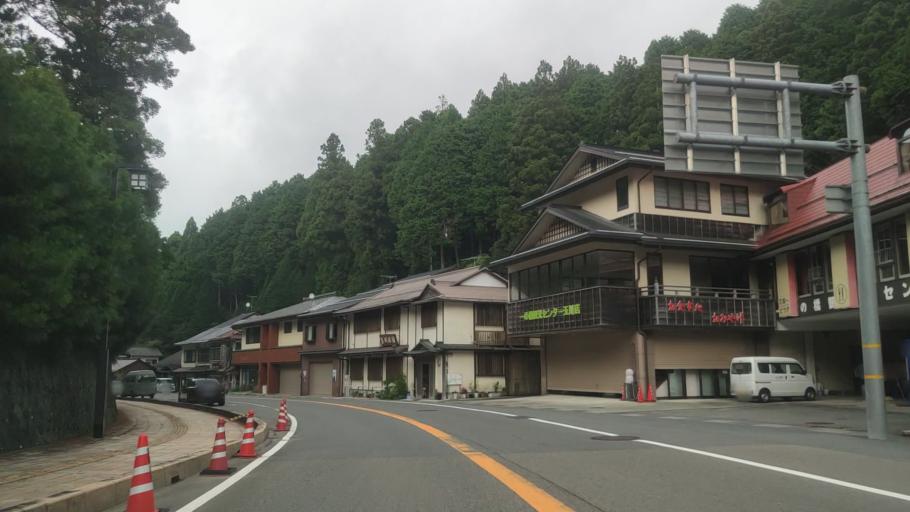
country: JP
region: Wakayama
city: Koya
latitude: 34.2145
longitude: 135.5982
